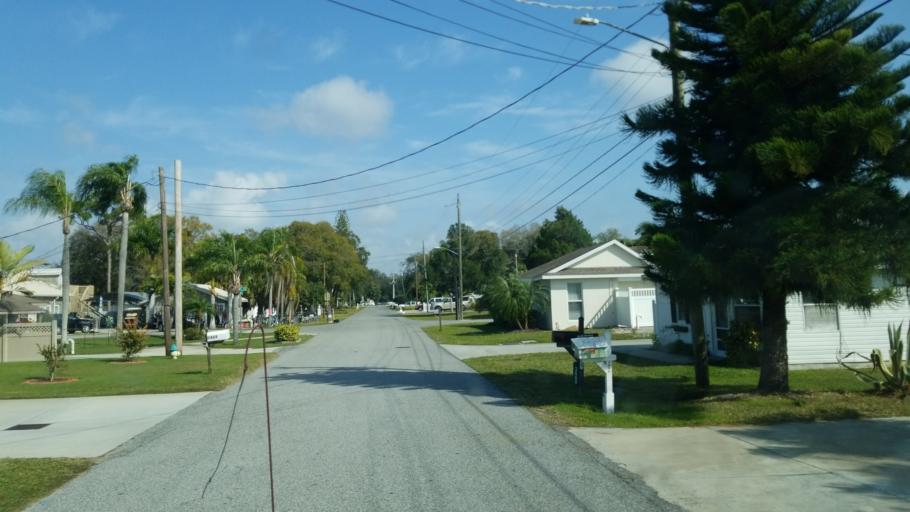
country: US
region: Florida
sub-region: Sarasota County
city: Southgate
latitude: 27.3217
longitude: -82.4989
